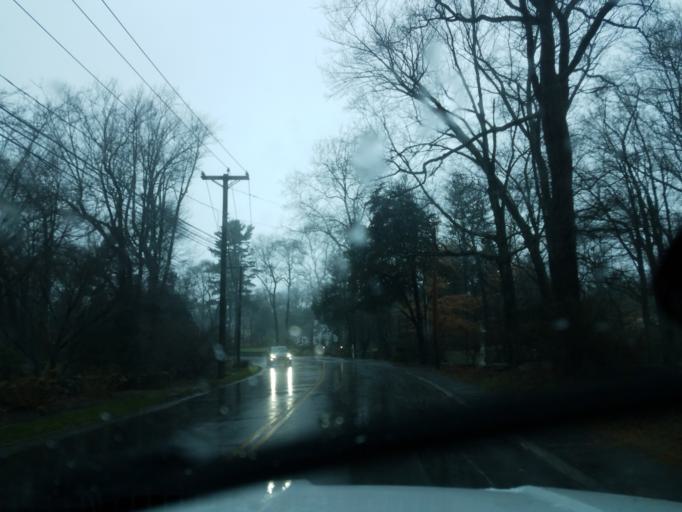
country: US
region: Connecticut
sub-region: Fairfield County
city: Darien
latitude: 41.0835
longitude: -73.4763
